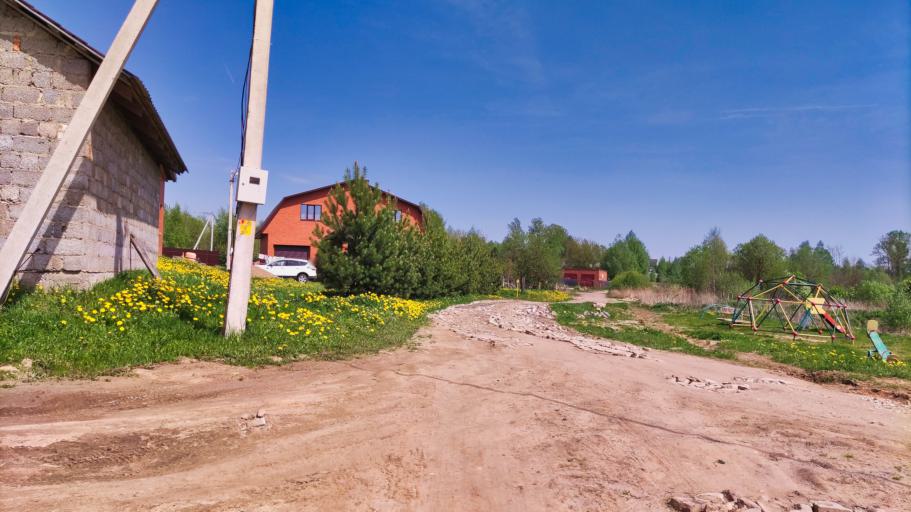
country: RU
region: Tverskaya
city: Rzhev
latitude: 56.2352
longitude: 34.3263
